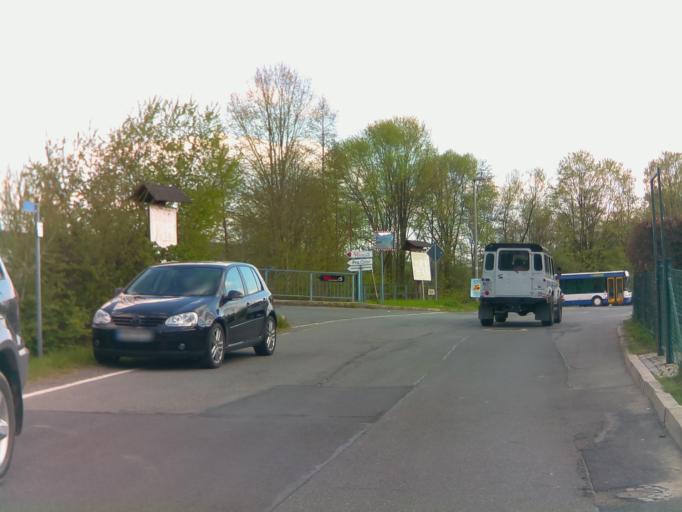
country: DE
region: Bavaria
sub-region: Upper Franconia
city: Pressig
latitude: 50.3570
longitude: 11.2774
